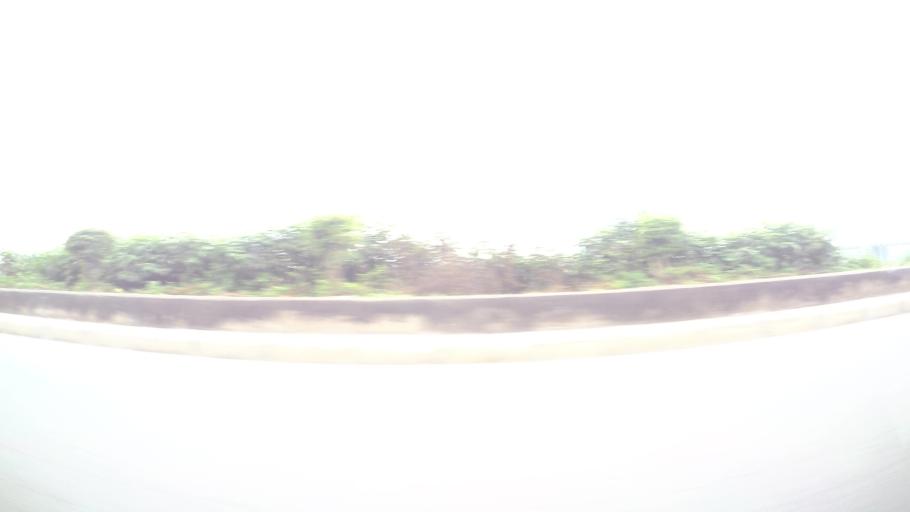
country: VN
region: Ha Noi
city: Hoan Kiem
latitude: 21.0681
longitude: 105.8754
